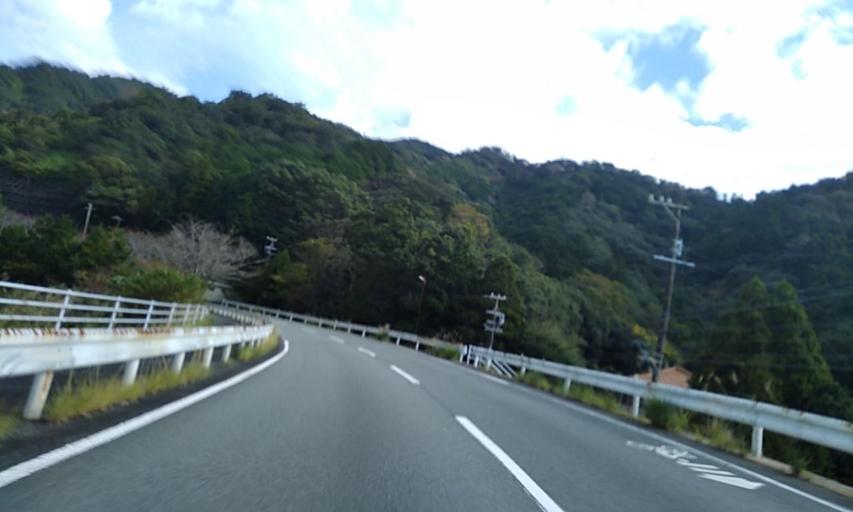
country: JP
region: Mie
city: Ise
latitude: 34.2564
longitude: 136.4707
